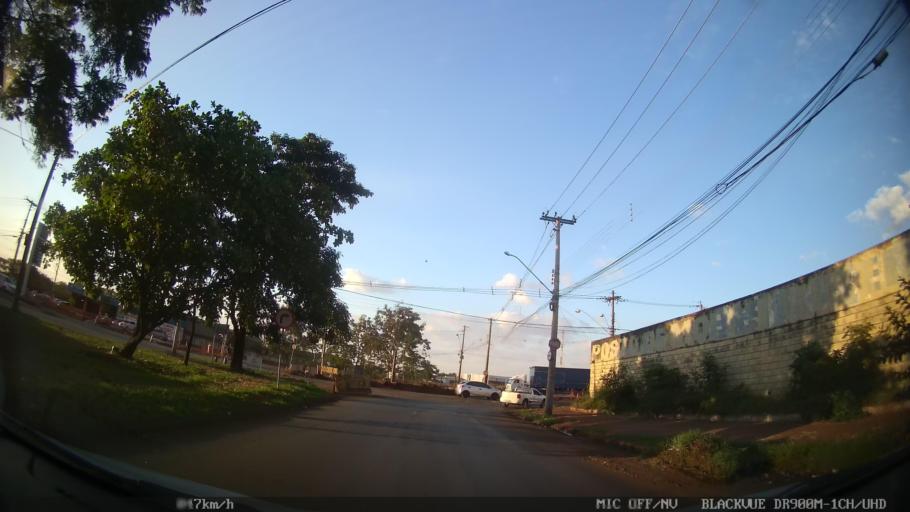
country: BR
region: Sao Paulo
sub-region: Ribeirao Preto
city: Ribeirao Preto
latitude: -21.1419
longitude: -47.7832
